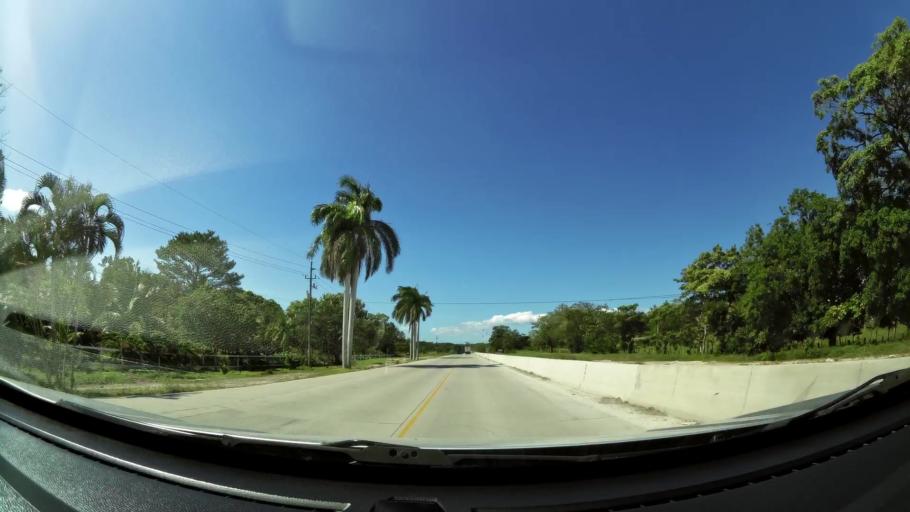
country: CR
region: Guanacaste
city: Liberia
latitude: 10.5625
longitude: -85.3836
